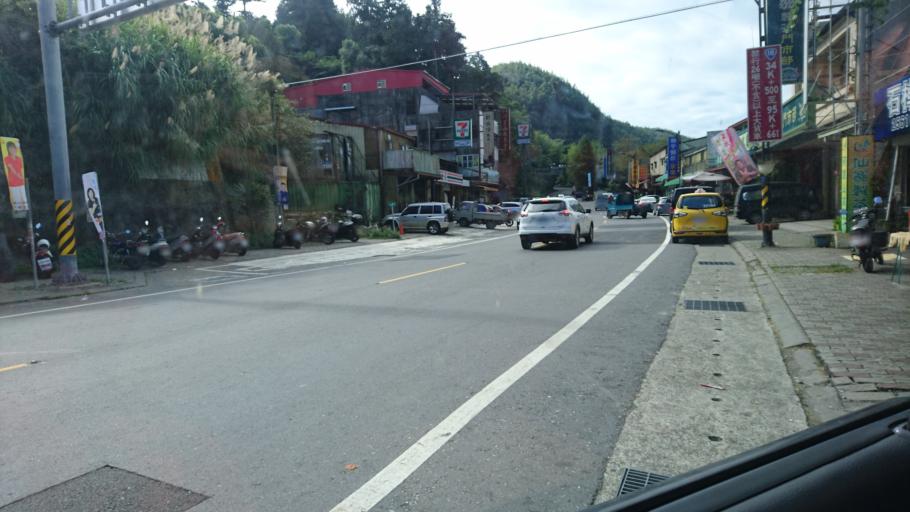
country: TW
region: Taiwan
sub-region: Chiayi
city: Jiayi Shi
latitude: 23.4731
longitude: 120.6972
